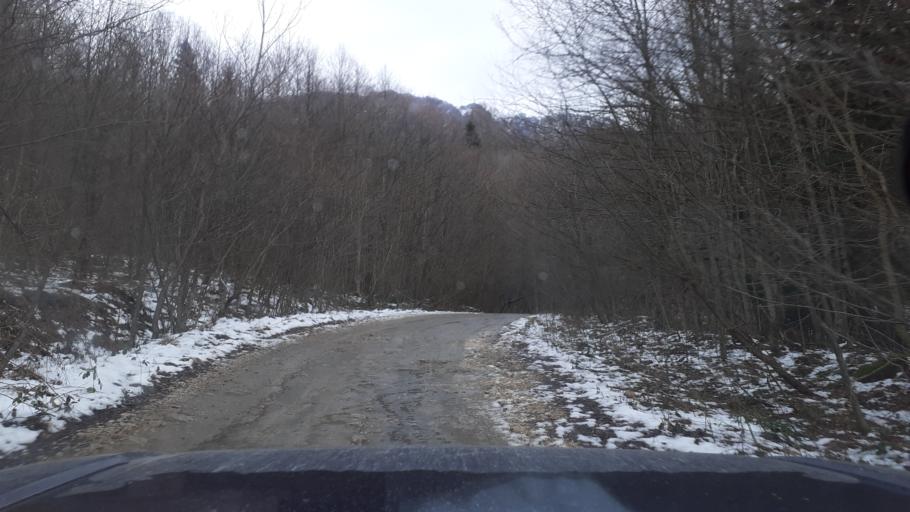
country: RU
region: Krasnodarskiy
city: Neftegorsk
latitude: 44.0809
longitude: 39.7412
